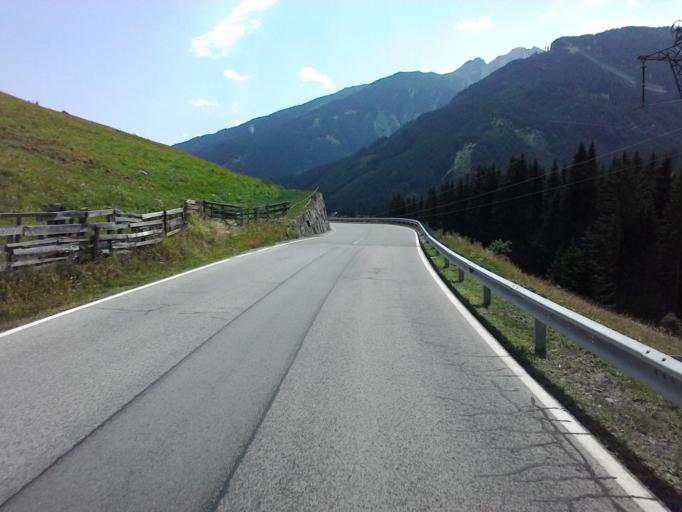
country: AT
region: Tyrol
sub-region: Politischer Bezirk Lienz
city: Obertilliach
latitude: 46.7022
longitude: 12.6459
